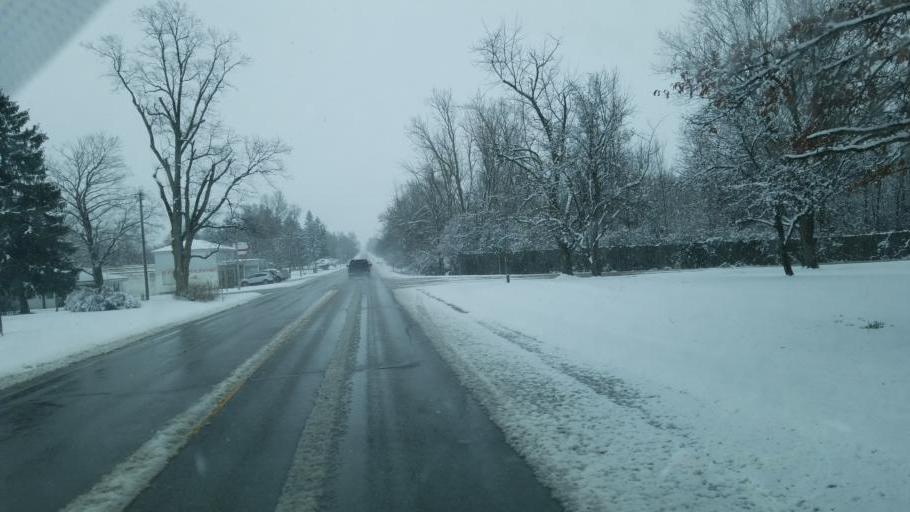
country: US
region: Indiana
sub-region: Delaware County
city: Muncie
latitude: 40.1137
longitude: -85.3222
